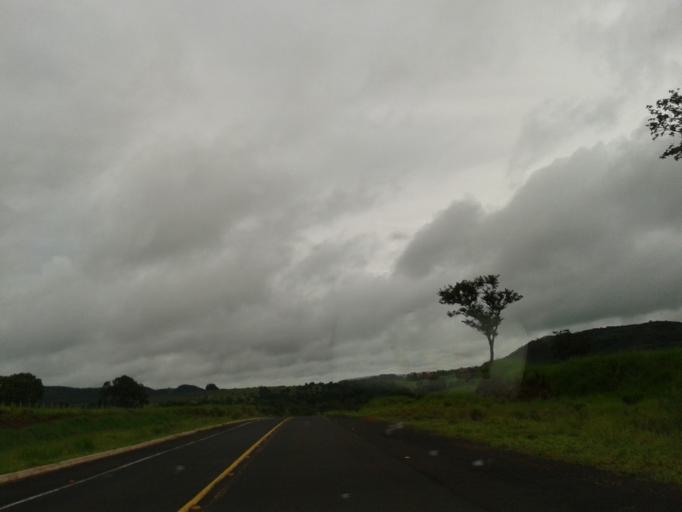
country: BR
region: Minas Gerais
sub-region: Santa Vitoria
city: Santa Vitoria
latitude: -19.2265
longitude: -50.0195
